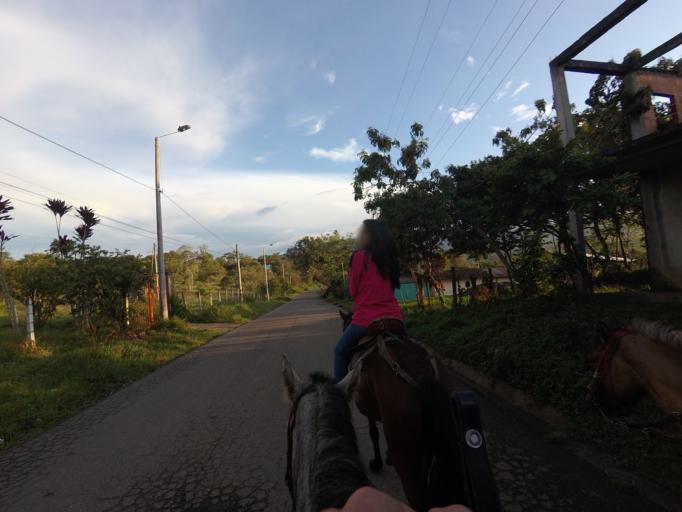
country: CO
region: Huila
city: San Agustin
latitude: 1.8911
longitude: -76.2718
